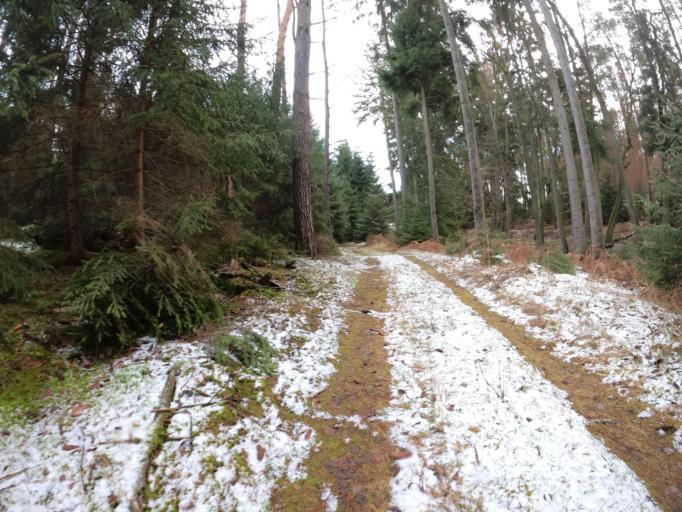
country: PL
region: Lubusz
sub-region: Powiat slubicki
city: Cybinka
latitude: 52.2570
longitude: 14.7980
